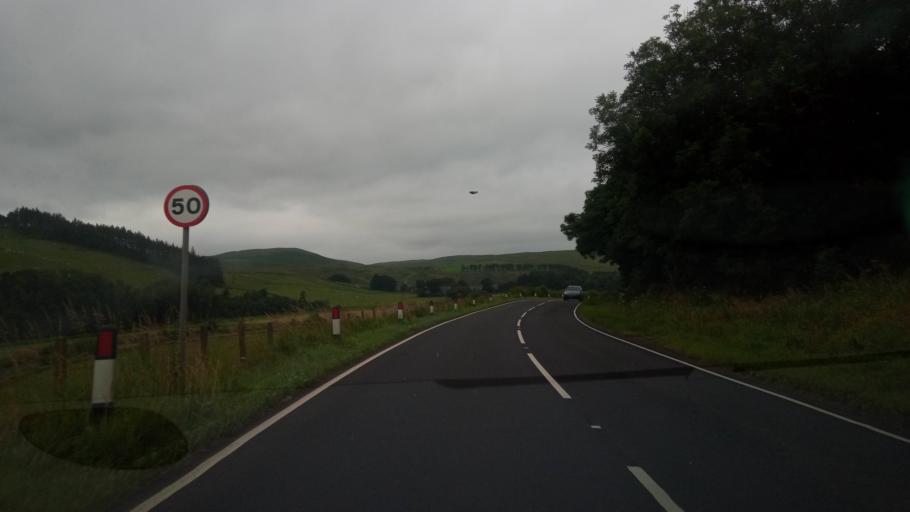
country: GB
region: Scotland
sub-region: The Scottish Borders
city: Hawick
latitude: 55.3671
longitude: -2.8812
